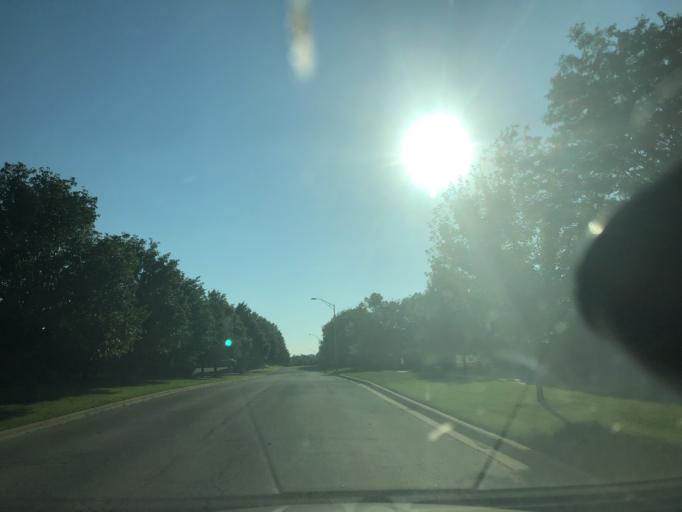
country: US
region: Illinois
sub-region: Will County
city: Mokena
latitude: 41.5571
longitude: -87.8926
